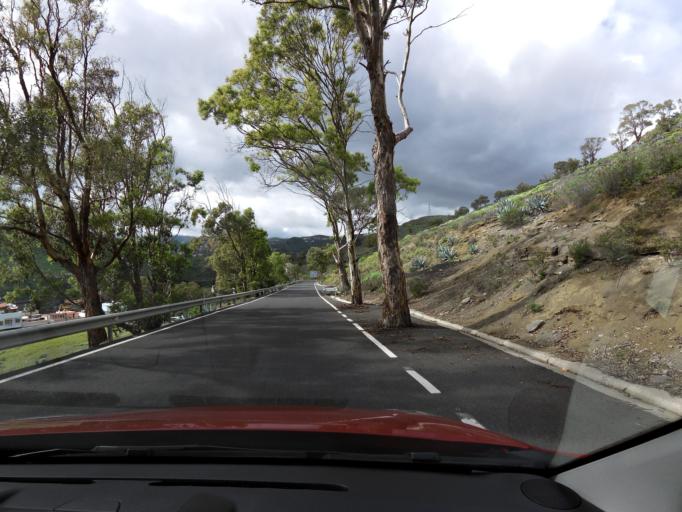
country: ES
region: Canary Islands
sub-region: Provincia de Las Palmas
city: Telde
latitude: 28.0121
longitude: -15.4385
